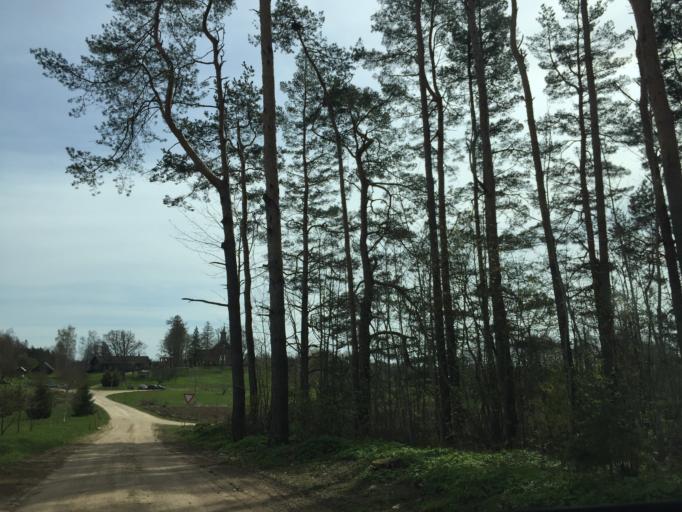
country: LV
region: Ludzas Rajons
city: Ludza
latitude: 56.5644
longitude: 27.5605
